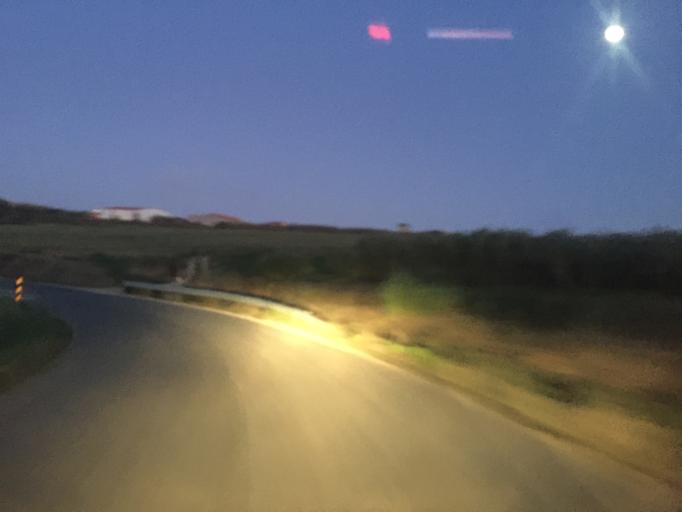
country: PT
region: Leiria
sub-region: Bombarral
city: Bombarral
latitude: 39.2800
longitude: -9.2293
